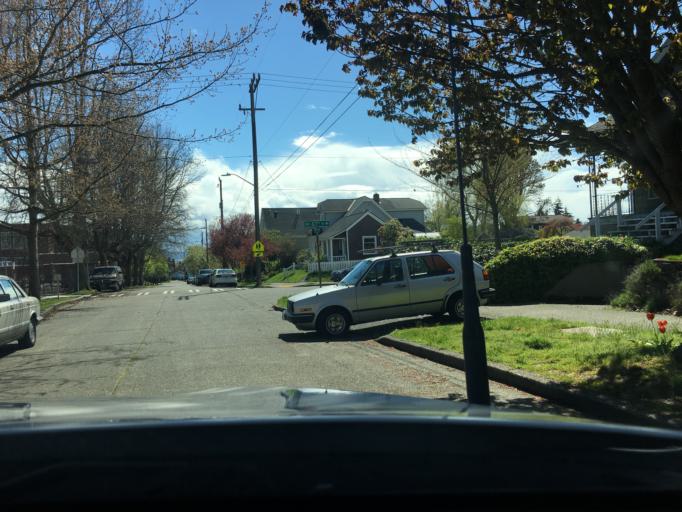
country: US
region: Washington
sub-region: King County
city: Seattle
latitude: 47.6780
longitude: -122.3811
